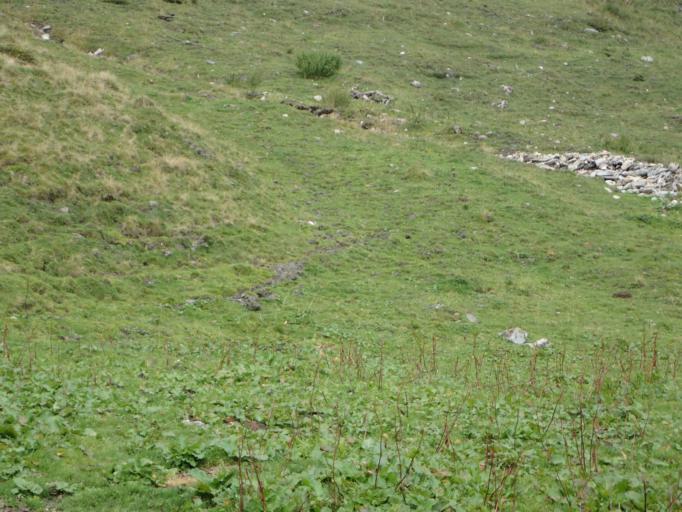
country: AT
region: Salzburg
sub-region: Politischer Bezirk Zell am See
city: Taxenbach
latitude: 47.2529
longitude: 12.9543
